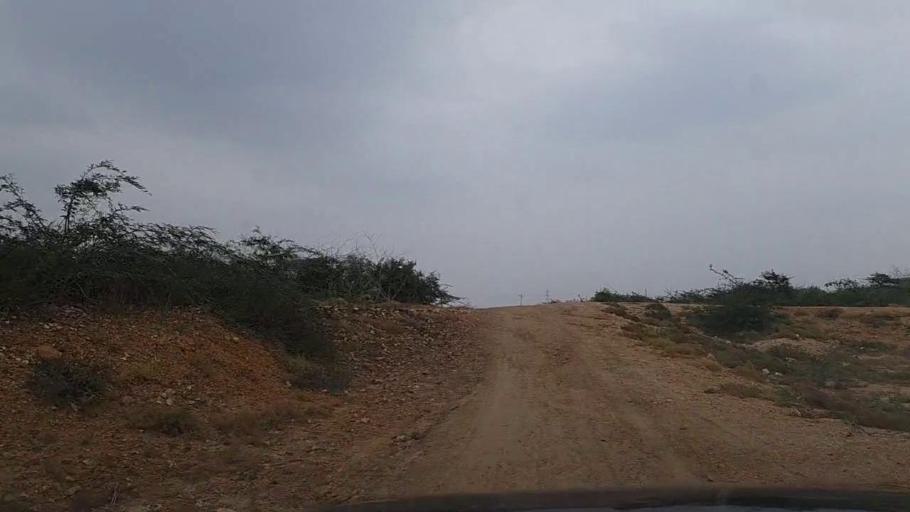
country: PK
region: Sindh
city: Thatta
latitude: 24.8170
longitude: 67.8327
